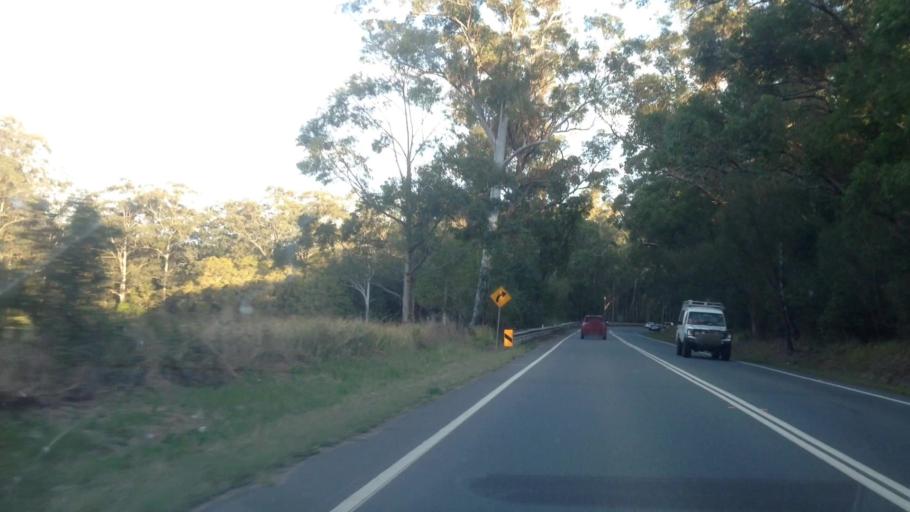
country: AU
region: New South Wales
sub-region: Lake Macquarie Shire
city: Dora Creek
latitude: -32.9948
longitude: 151.4911
